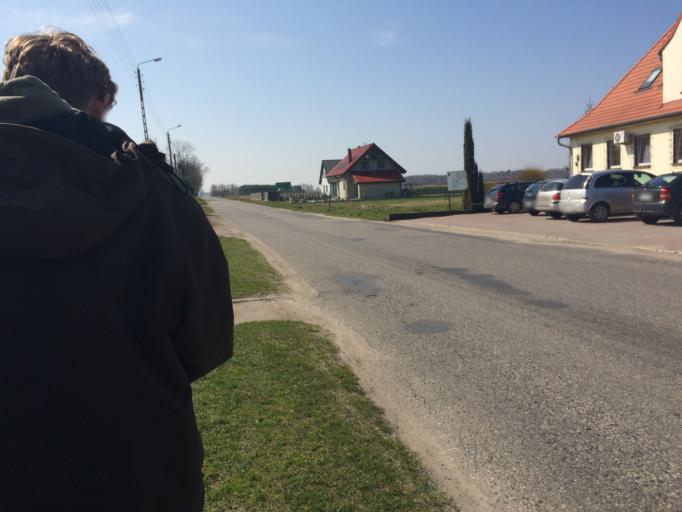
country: PL
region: Lower Silesian Voivodeship
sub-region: Powiat olesnicki
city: Dziadowa Kloda
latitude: 51.2327
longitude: 17.7029
